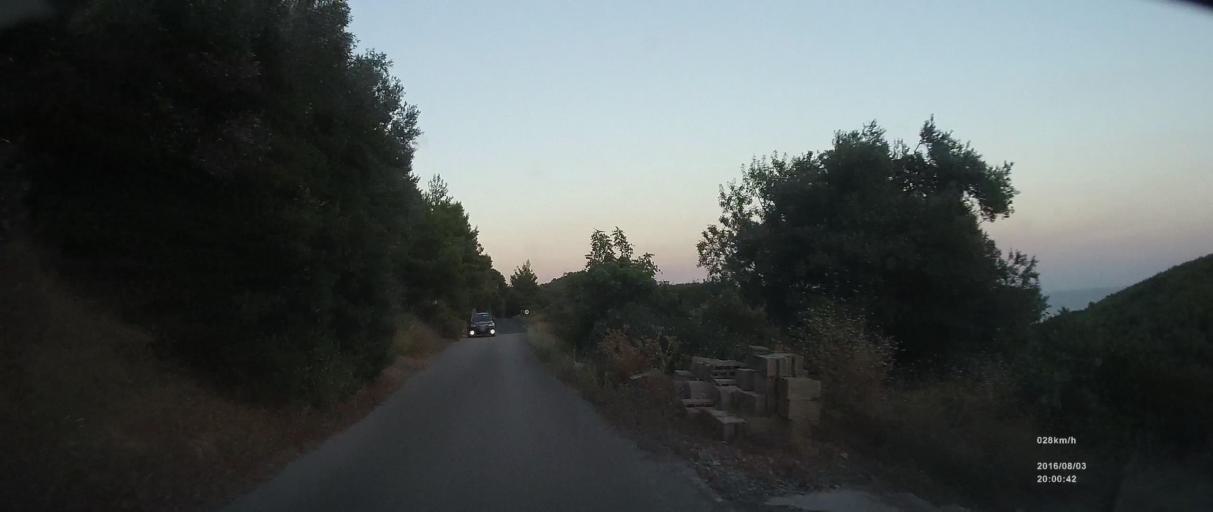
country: HR
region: Dubrovacko-Neretvanska
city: Blato
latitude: 42.7318
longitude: 17.5650
